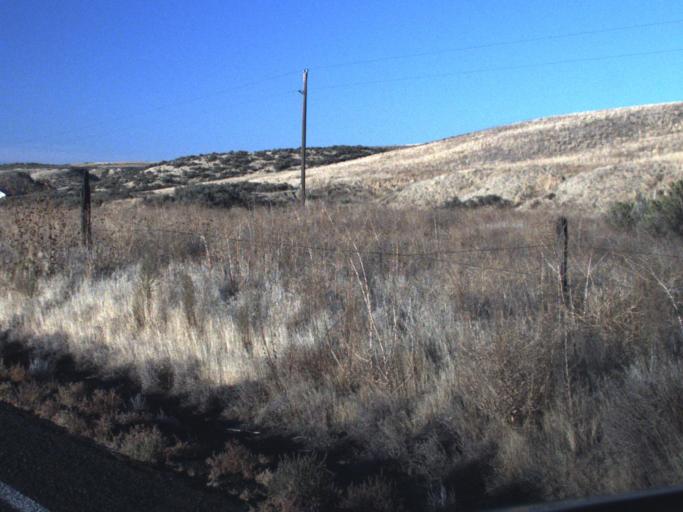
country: US
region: Washington
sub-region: Adams County
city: Ritzville
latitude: 46.6889
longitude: -118.3888
